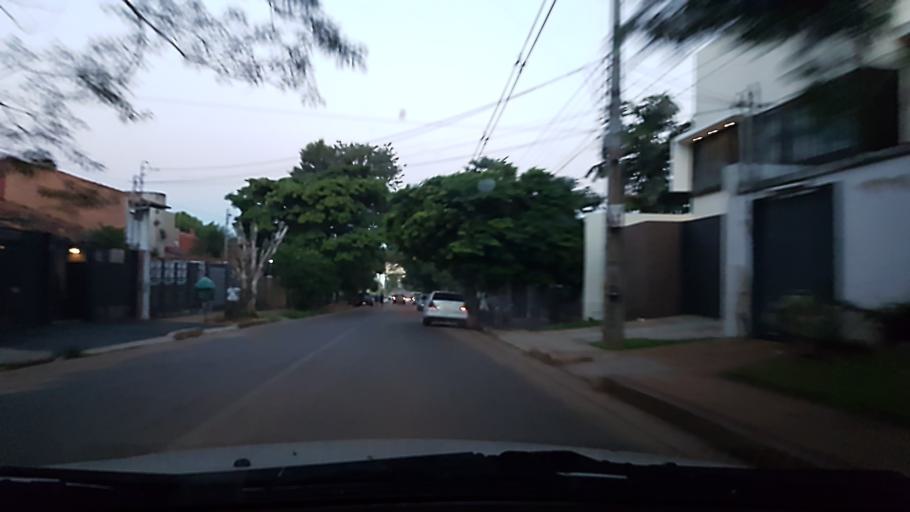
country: PY
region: Central
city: Fernando de la Mora
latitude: -25.3086
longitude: -57.5571
